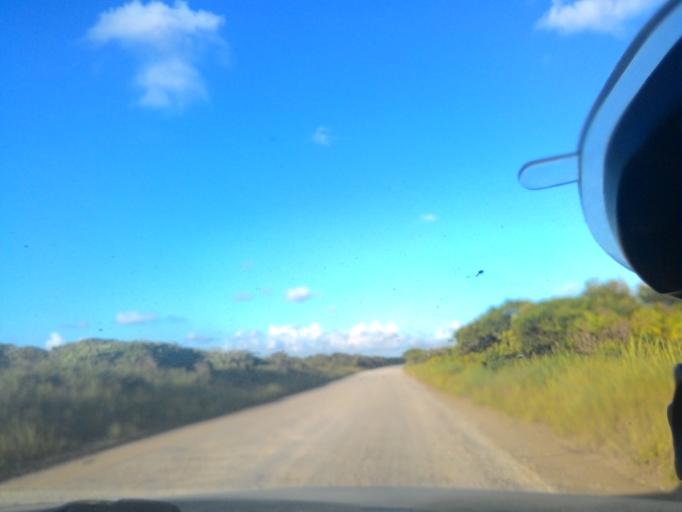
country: BR
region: Sao Paulo
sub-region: Iguape
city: Iguape
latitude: -24.8584
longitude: -47.7080
